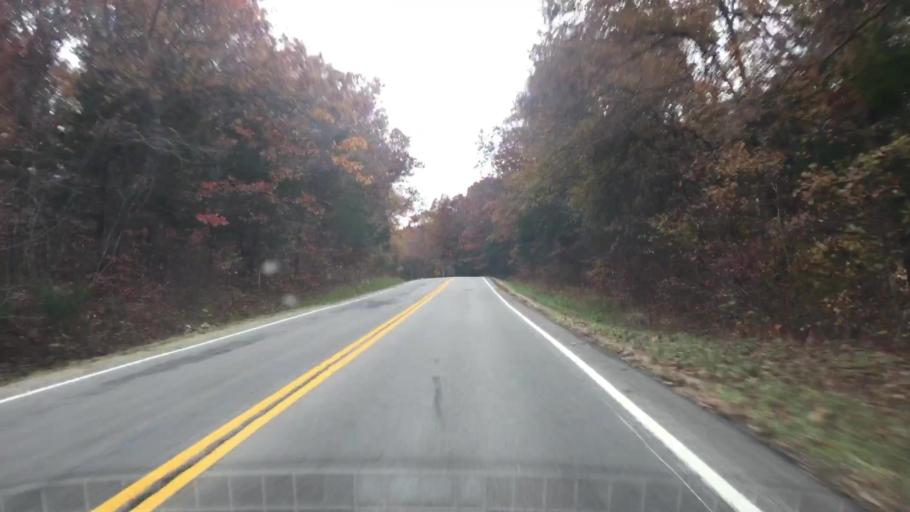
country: US
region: Missouri
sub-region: Gasconade County
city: Hermann
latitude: 38.7233
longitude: -91.6966
